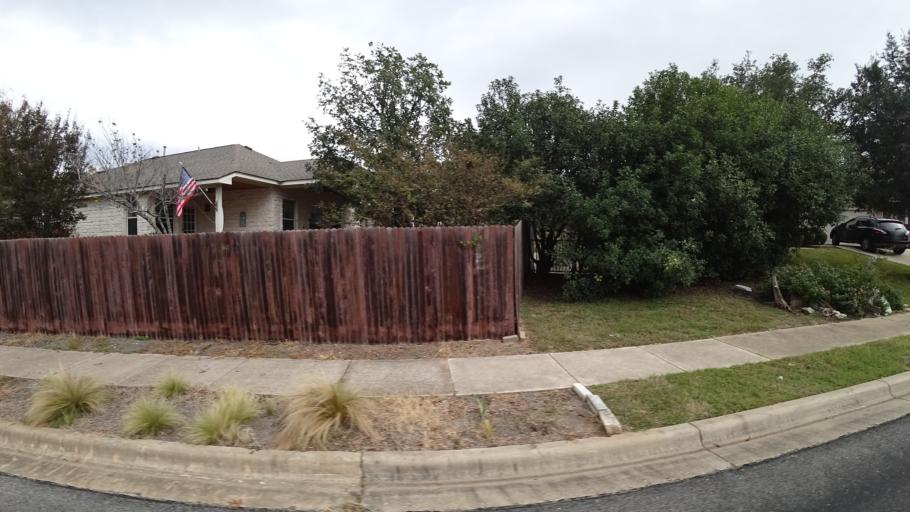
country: US
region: Texas
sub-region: Williamson County
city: Brushy Creek
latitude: 30.5070
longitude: -97.7486
